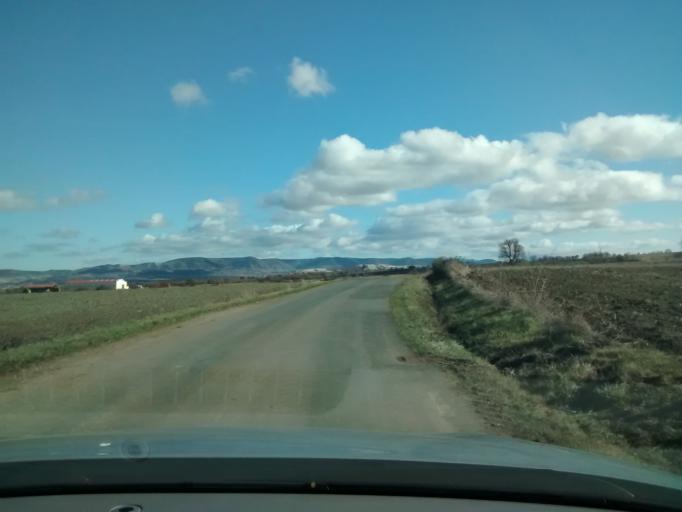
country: ES
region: Castille and Leon
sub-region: Provincia de Burgos
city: Medina de Pomar
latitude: 42.8970
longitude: -3.5537
